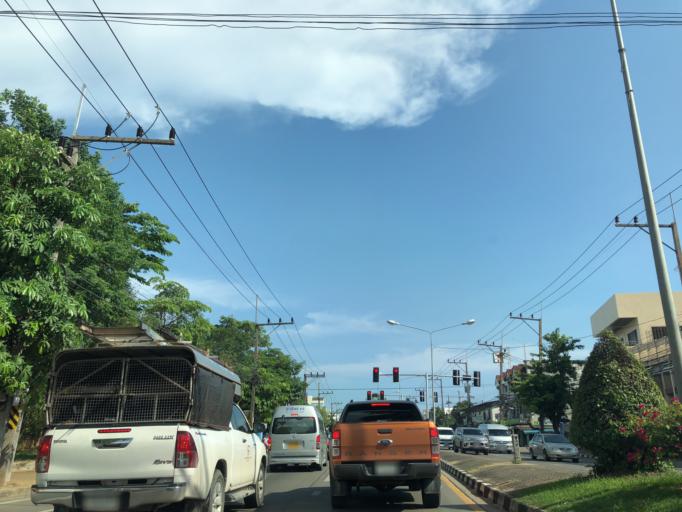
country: TH
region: Krabi
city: Krabi
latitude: 8.0811
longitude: 98.9149
